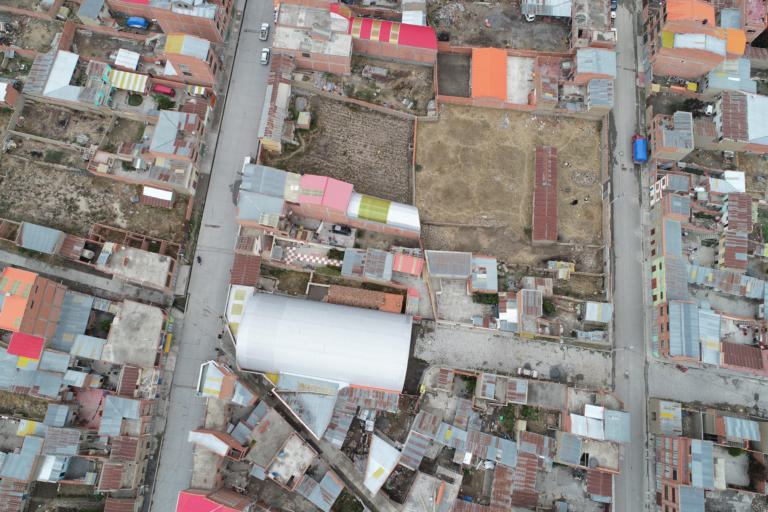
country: BO
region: La Paz
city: Achacachi
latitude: -16.0476
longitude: -68.6836
